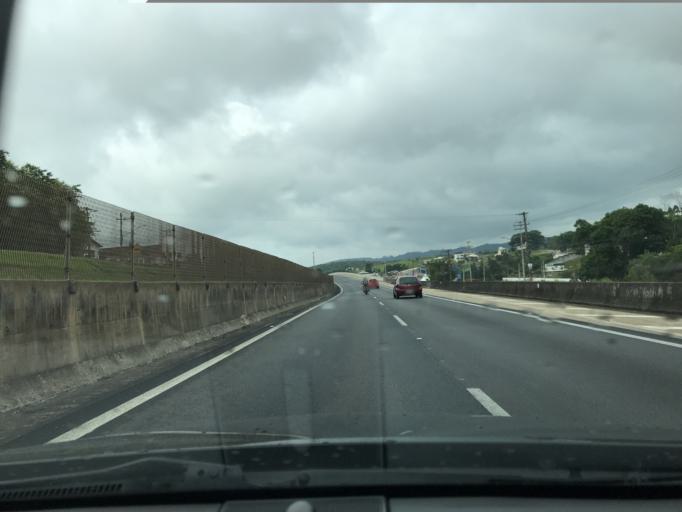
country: BR
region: Sao Paulo
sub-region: Vargem Grande Paulista
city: Vargem Grande Paulista
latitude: -23.6066
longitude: -47.0137
